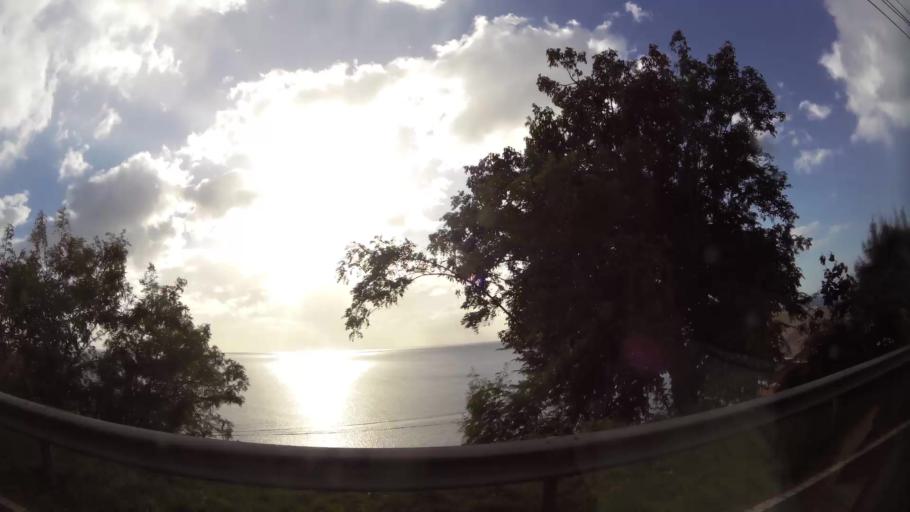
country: DM
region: Saint Paul
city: Mahaut
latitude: 15.3572
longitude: -61.3957
